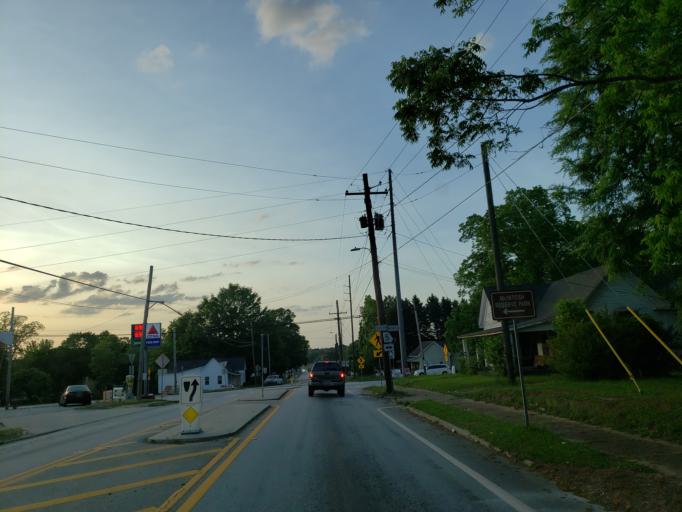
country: US
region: Georgia
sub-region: Coweta County
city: Newnan
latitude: 33.4909
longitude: -84.9120
